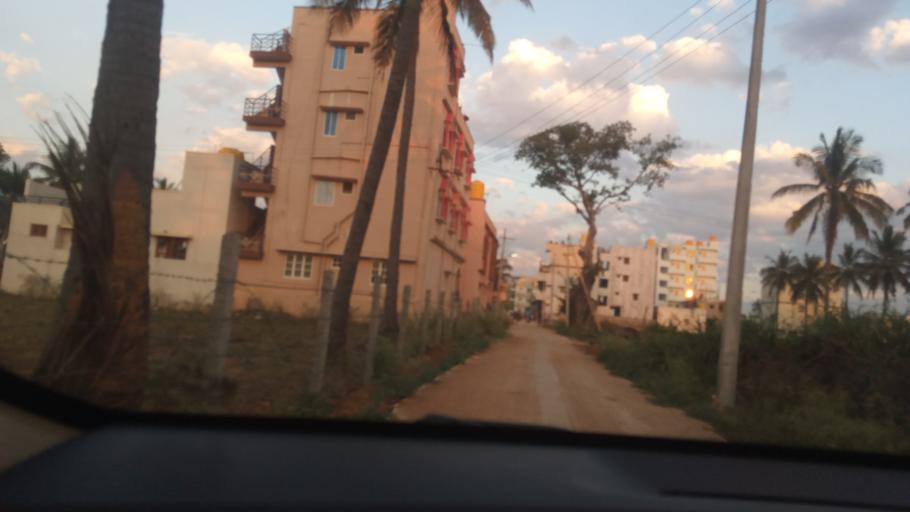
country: IN
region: Karnataka
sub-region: Bangalore Rural
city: Hoskote
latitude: 12.9794
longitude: 77.7994
